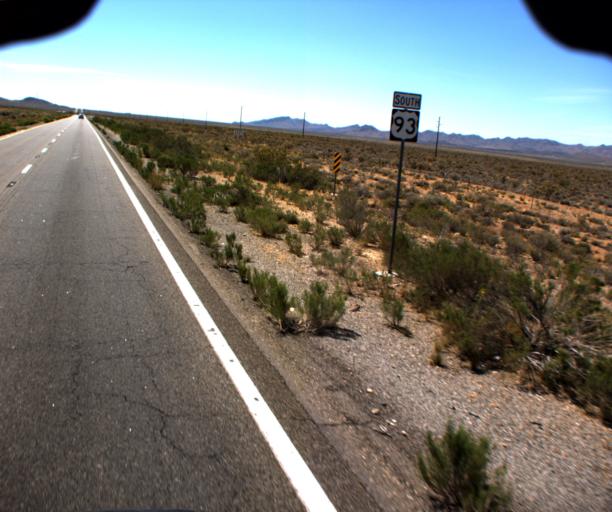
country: US
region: Arizona
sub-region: Mohave County
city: Dolan Springs
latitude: 35.4809
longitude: -114.3190
